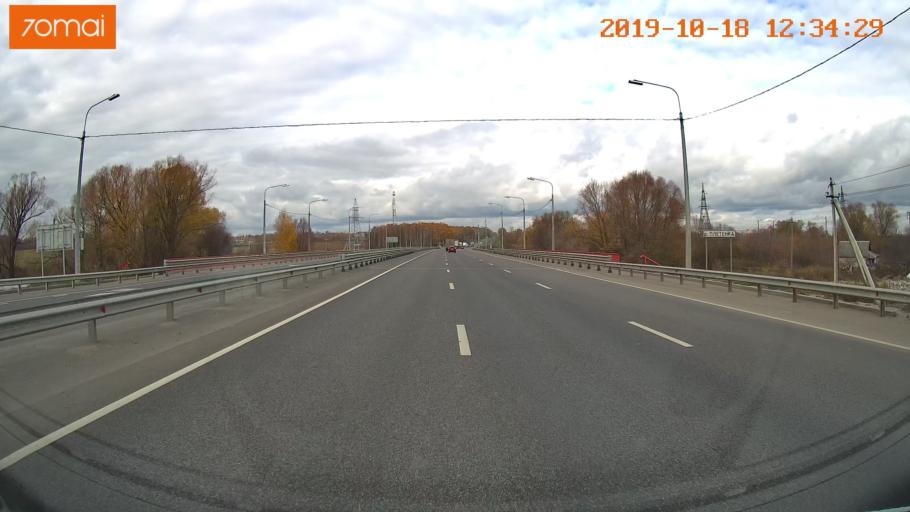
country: RU
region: Rjazan
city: Ryazan'
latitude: 54.6146
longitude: 39.6383
